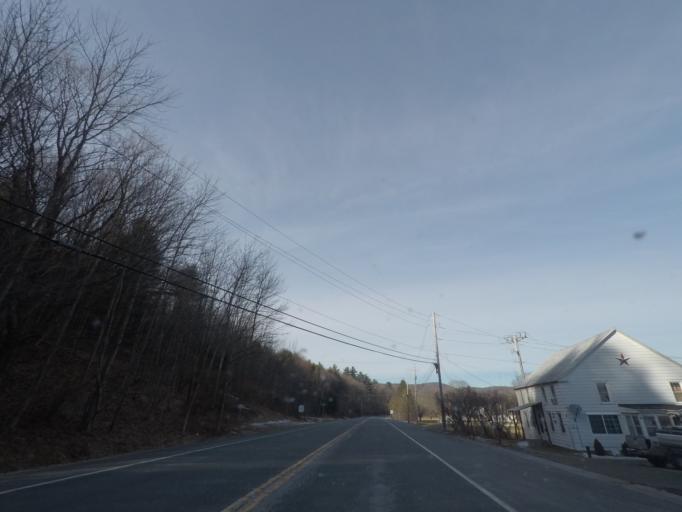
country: US
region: Massachusetts
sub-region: Berkshire County
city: Williamstown
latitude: 42.6997
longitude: -73.3768
